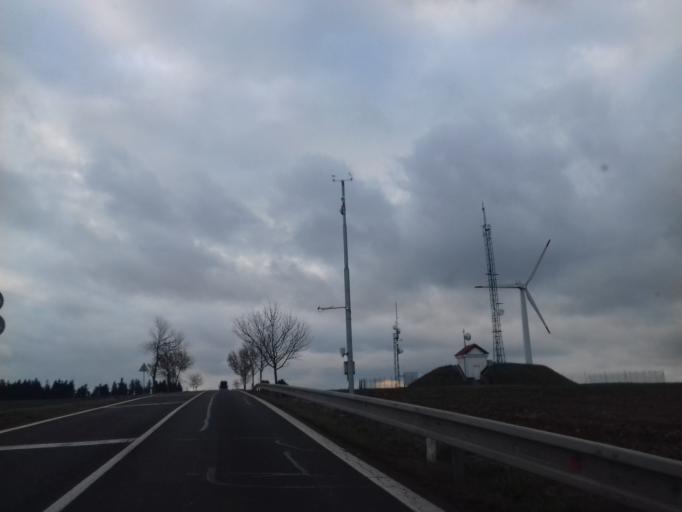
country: CZ
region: Pardubicky
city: Radimer
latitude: 49.7411
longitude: 16.3927
